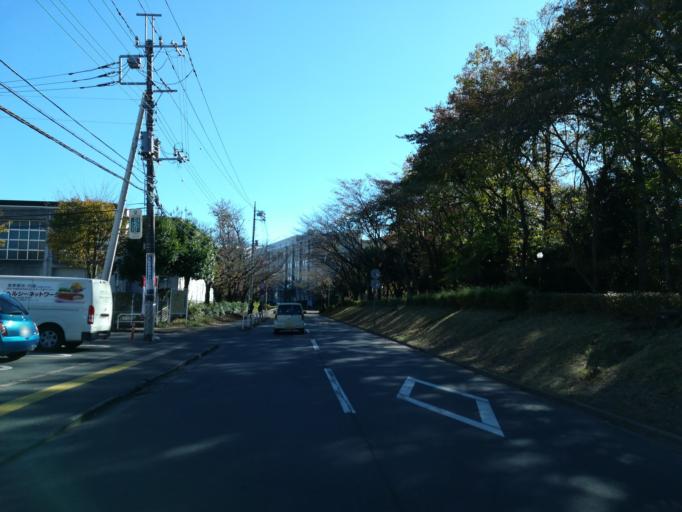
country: JP
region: Ibaraki
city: Naka
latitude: 36.0940
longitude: 140.1069
